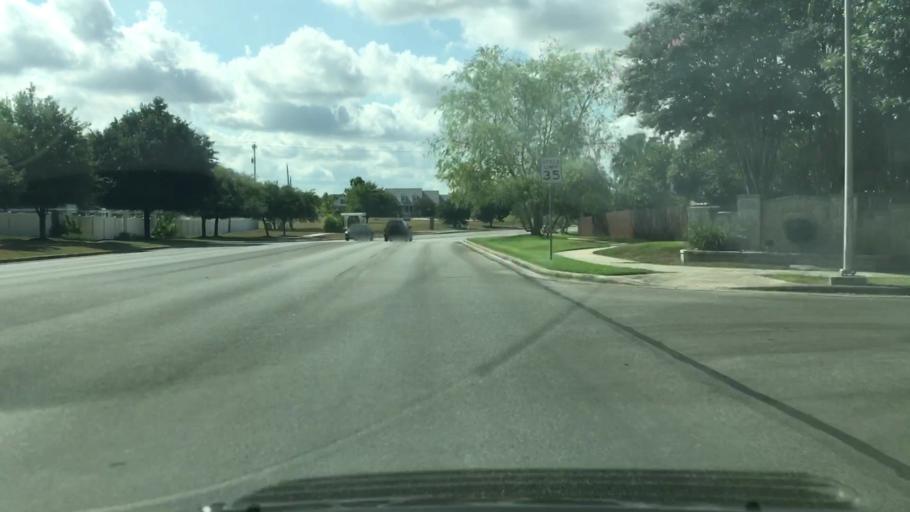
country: US
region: Texas
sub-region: Guadalupe County
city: Cibolo
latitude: 29.5913
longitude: -98.2497
